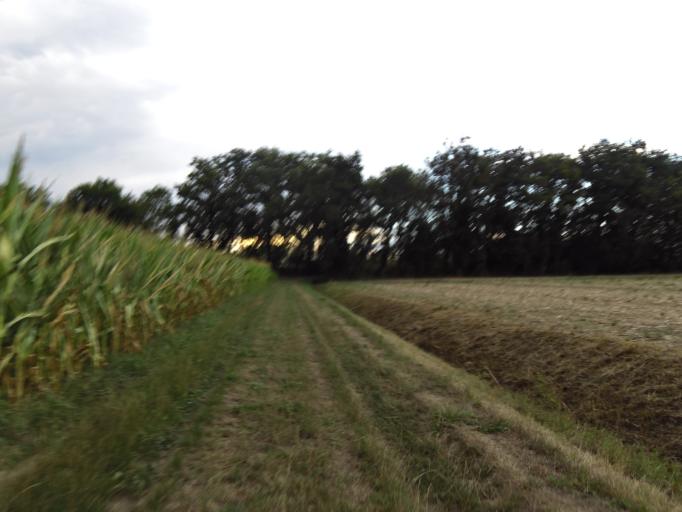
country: FR
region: Rhone-Alpes
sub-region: Departement de l'Ain
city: Perouges
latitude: 45.9438
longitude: 5.1680
